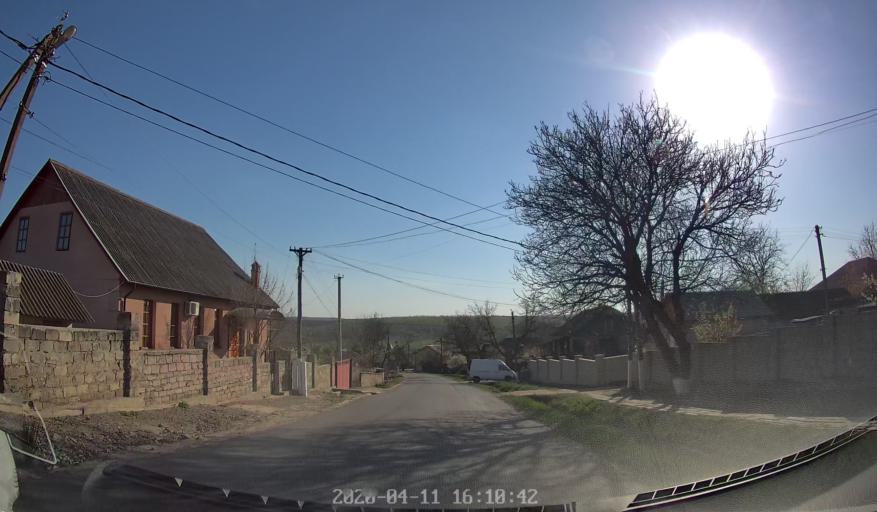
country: MD
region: Chisinau
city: Vadul lui Voda
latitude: 47.0665
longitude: 29.1323
